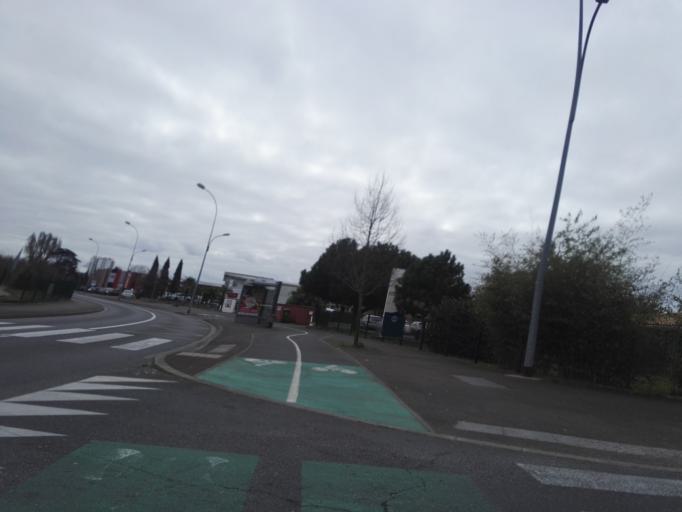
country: FR
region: Aquitaine
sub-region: Departement de la Gironde
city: Talence
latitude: 44.7877
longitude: -0.5811
